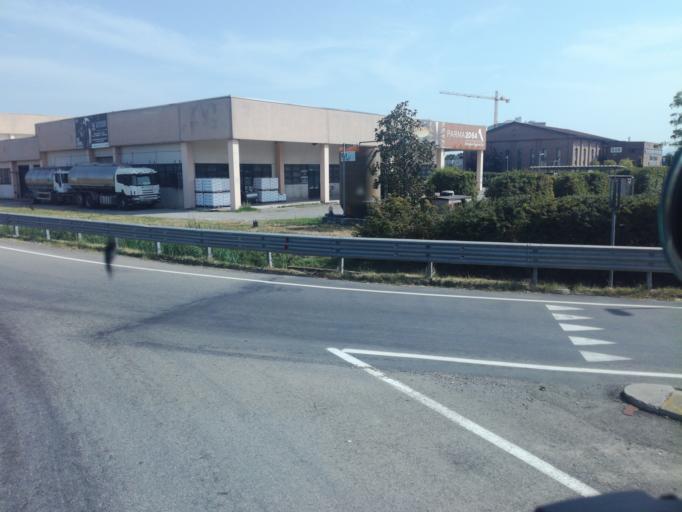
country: IT
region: Emilia-Romagna
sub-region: Provincia di Parma
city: Fidenza
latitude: 44.8859
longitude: 10.0861
